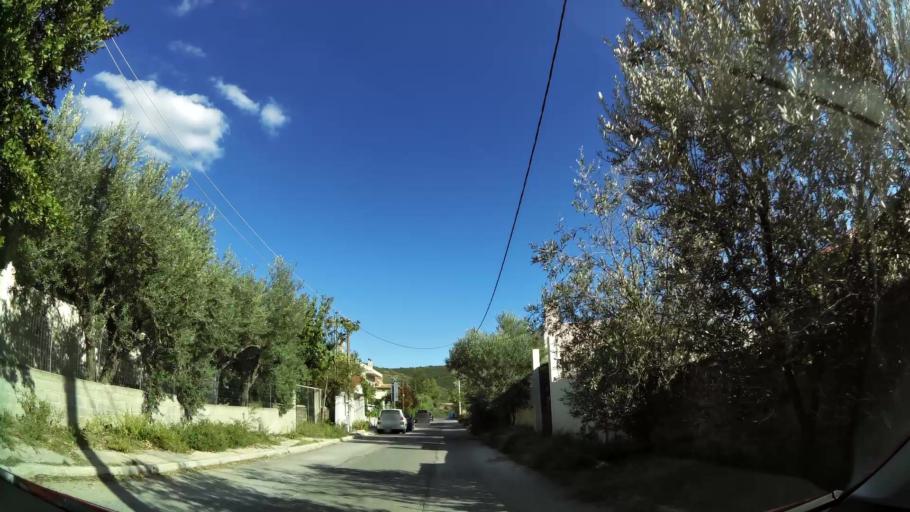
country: GR
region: Attica
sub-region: Nomarchia Anatolikis Attikis
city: Anthousa
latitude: 38.0263
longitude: 23.8780
